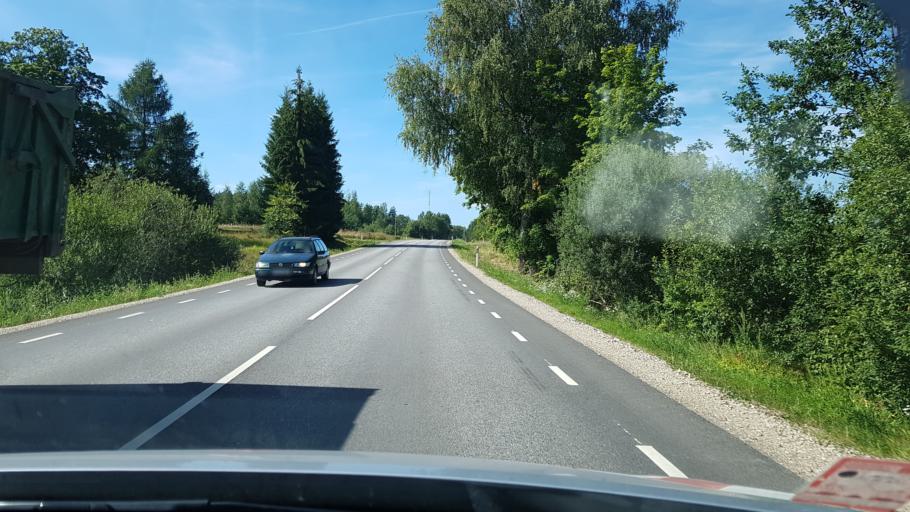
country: EE
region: Polvamaa
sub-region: Polva linn
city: Polva
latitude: 58.0106
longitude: 27.1846
